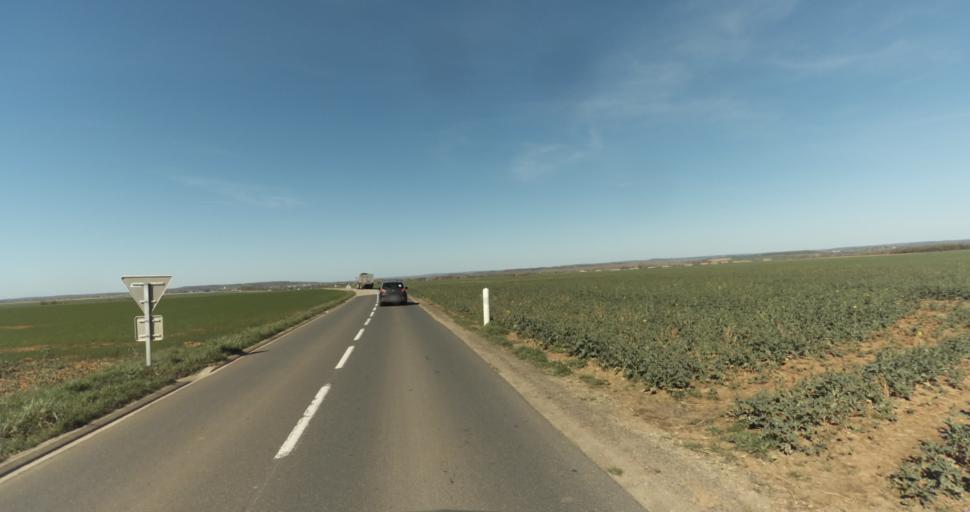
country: FR
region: Lower Normandy
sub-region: Departement du Calvados
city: Saint-Pierre-sur-Dives
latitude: 49.0350
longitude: -0.0643
